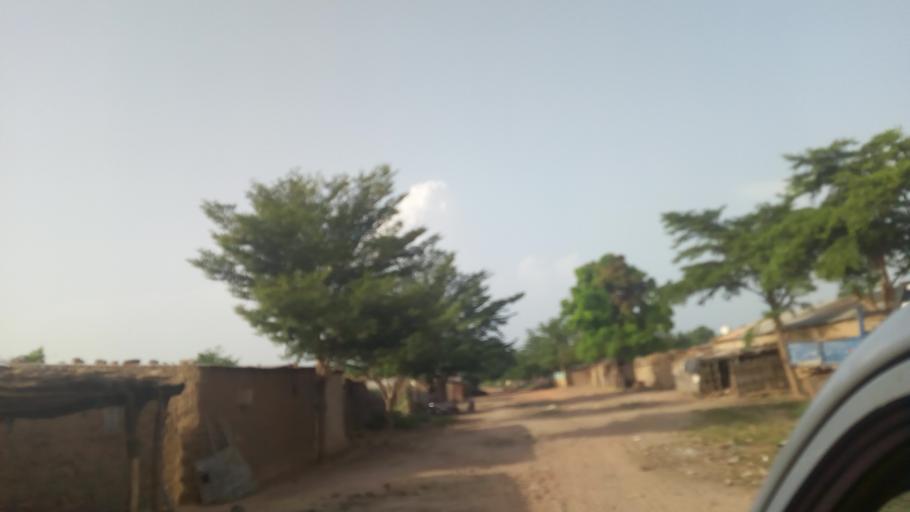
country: ML
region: Kayes
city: Kita
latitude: 13.1340
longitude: -8.8307
